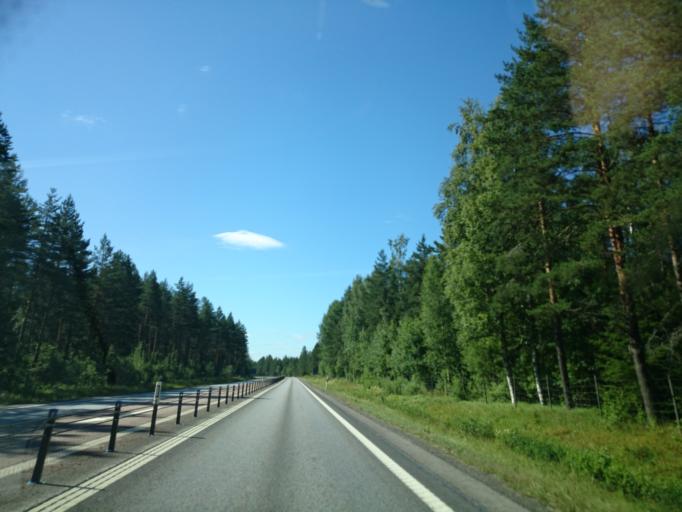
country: SE
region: Gaevleborg
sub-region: Gavle Kommun
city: Norrsundet
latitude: 61.0560
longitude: 16.9598
